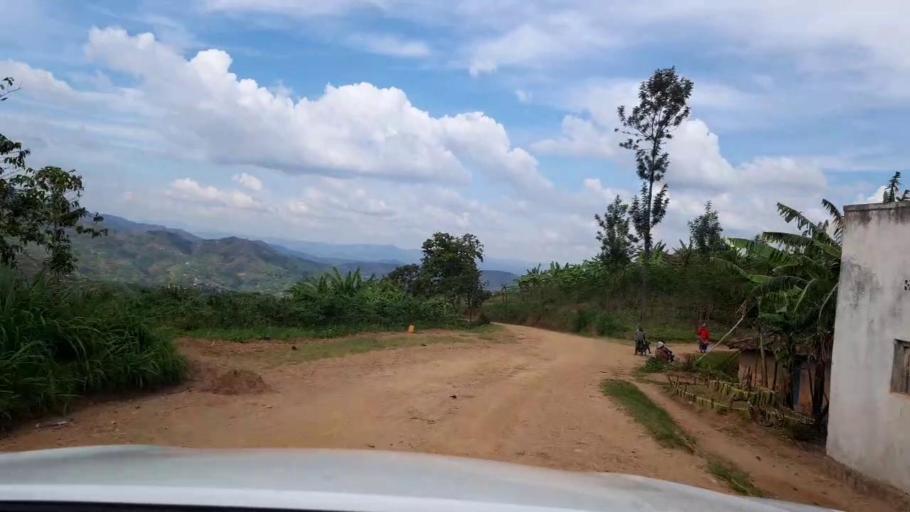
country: RW
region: Southern Province
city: Gitarama
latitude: -1.9833
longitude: 29.7105
